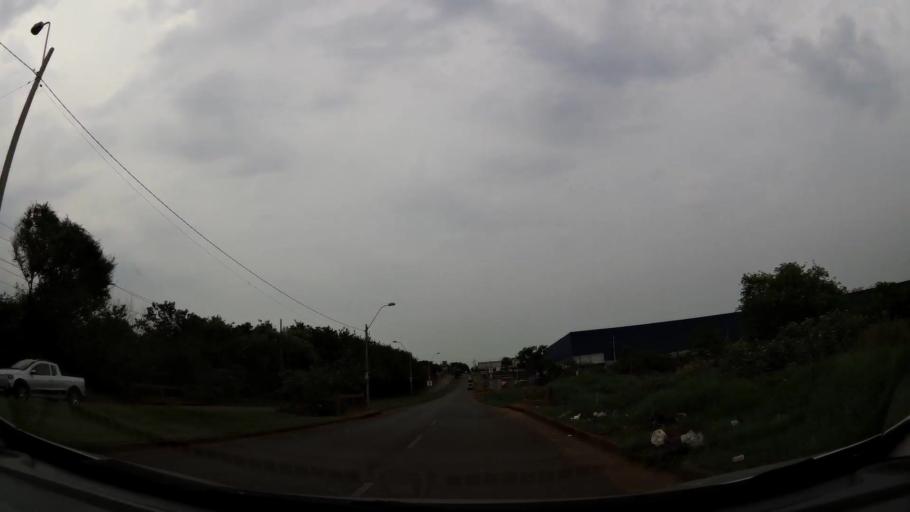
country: PY
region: Alto Parana
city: Presidente Franco
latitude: -25.5305
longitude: -54.6481
